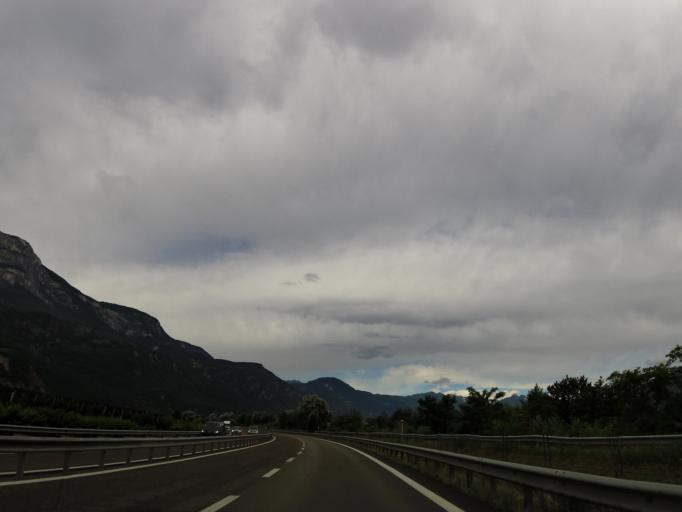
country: IT
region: Trentino-Alto Adige
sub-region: Bolzano
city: San Paolo
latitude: 46.4966
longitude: 11.2791
